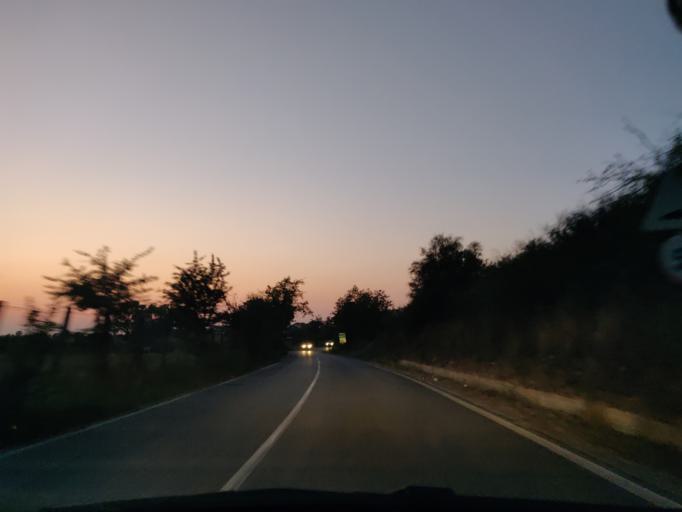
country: IT
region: Latium
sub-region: Citta metropolitana di Roma Capitale
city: Npp 23 (Parco Leonardo)
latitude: 41.8345
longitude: 12.2829
